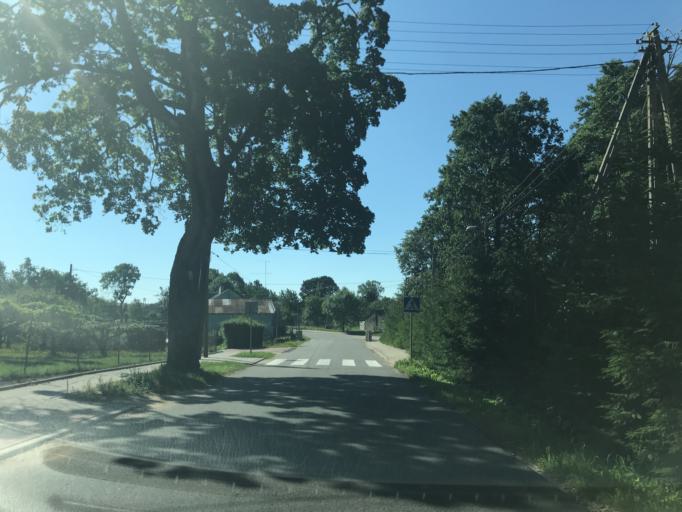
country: PL
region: Warmian-Masurian Voivodeship
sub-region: Powiat ostrodzki
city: Ostroda
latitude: 53.5771
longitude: 19.9177
